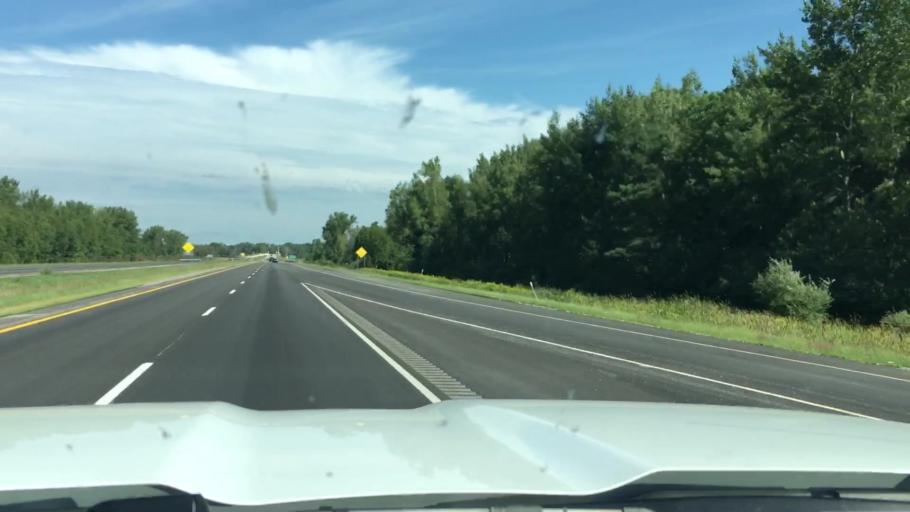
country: US
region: Michigan
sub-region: Saginaw County
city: Freeland
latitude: 43.5869
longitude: -84.1393
